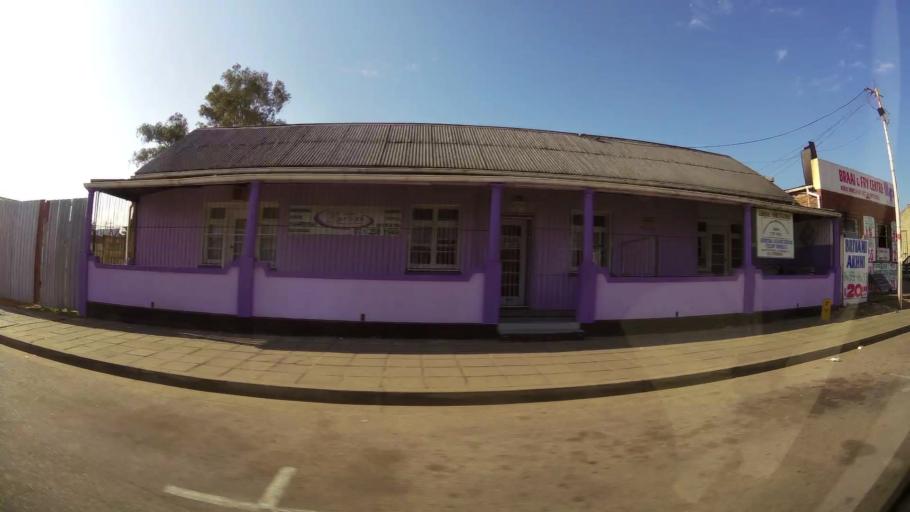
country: ZA
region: Eastern Cape
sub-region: Nelson Mandela Bay Metropolitan Municipality
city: Uitenhage
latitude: -33.7626
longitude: 25.3936
